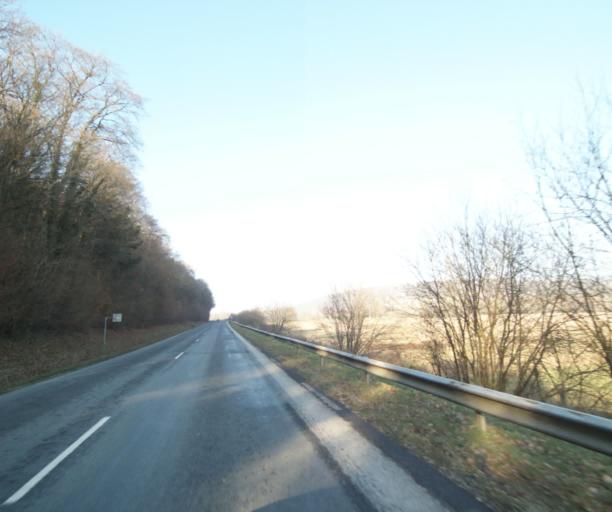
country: FR
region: Champagne-Ardenne
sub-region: Departement de la Haute-Marne
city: Chevillon
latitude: 48.5154
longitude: 5.1101
